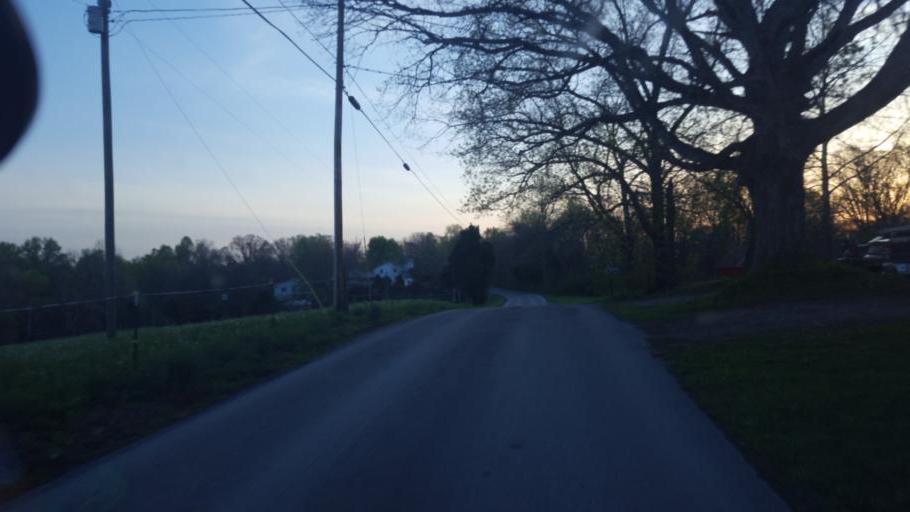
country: US
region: Kentucky
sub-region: Hart County
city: Munfordville
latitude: 37.2740
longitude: -85.9362
